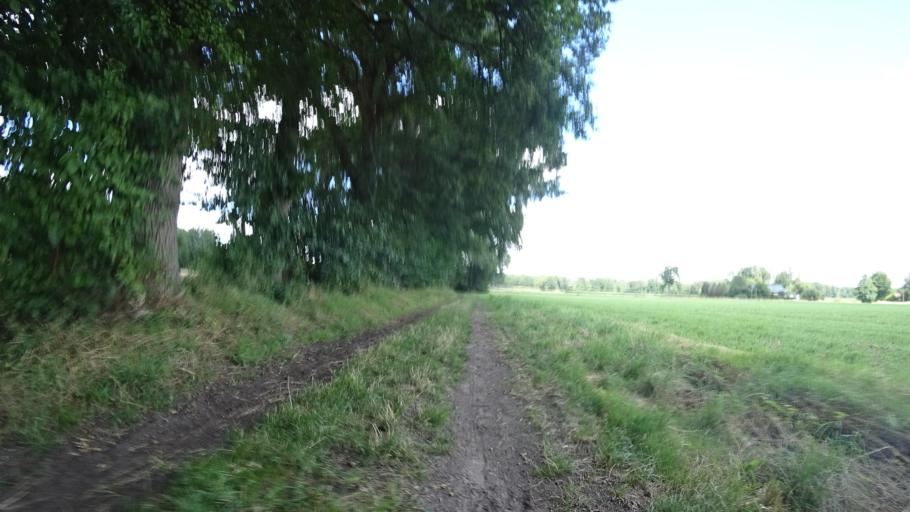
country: DE
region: North Rhine-Westphalia
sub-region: Regierungsbezirk Detmold
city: Guetersloh
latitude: 51.9355
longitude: 8.3925
